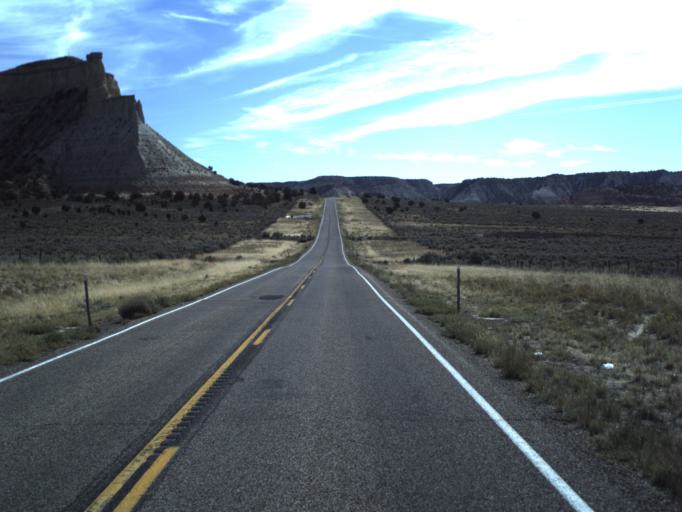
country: US
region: Utah
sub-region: Garfield County
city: Panguitch
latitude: 37.5614
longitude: -112.0289
